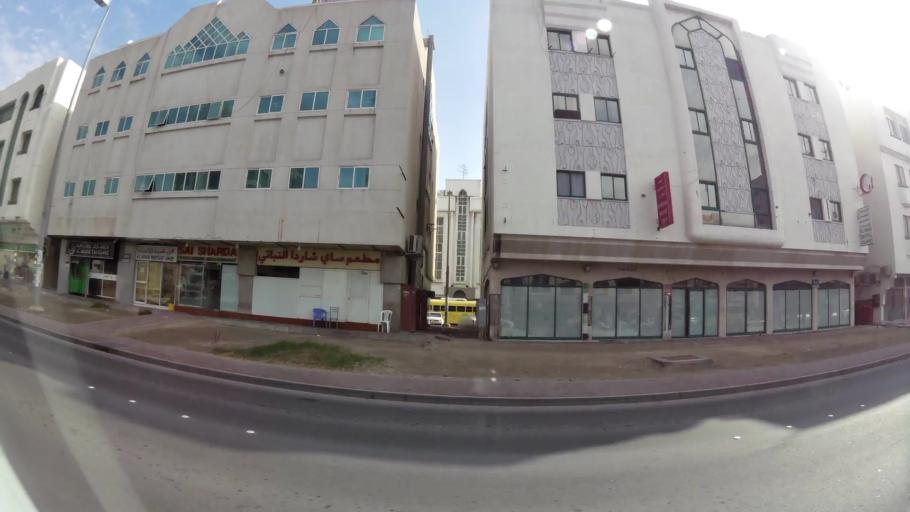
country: AE
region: Abu Dhabi
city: Abu Dhabi
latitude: 24.3246
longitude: 54.5345
